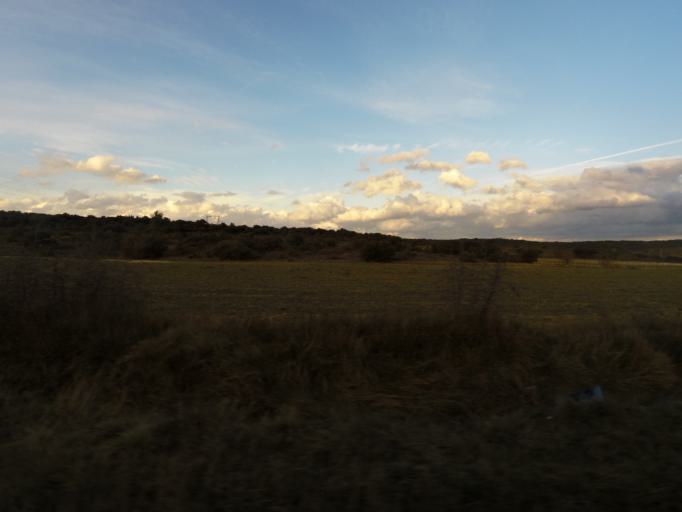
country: FR
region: Languedoc-Roussillon
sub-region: Departement du Gard
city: La Calmette
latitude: 43.8881
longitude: 4.2461
